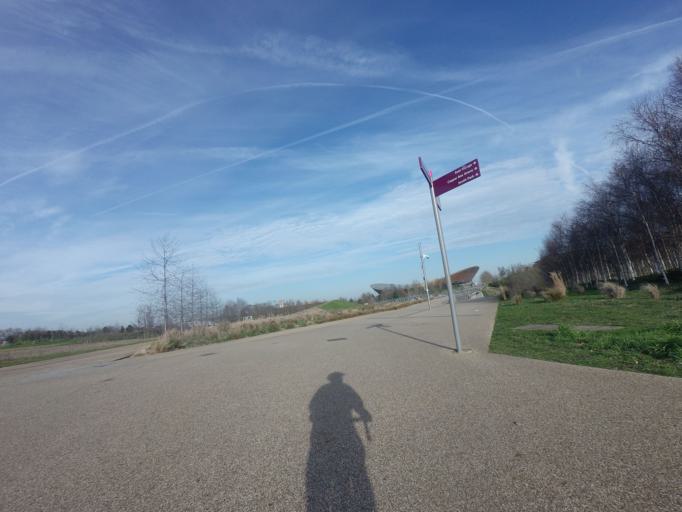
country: GB
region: England
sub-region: Greater London
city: Hackney
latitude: 51.5481
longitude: -0.0191
